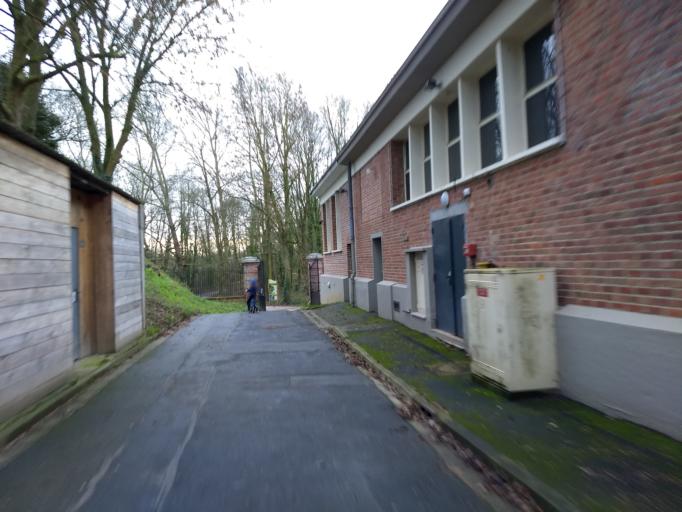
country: FR
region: Nord-Pas-de-Calais
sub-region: Departement du Pas-de-Calais
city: Achicourt
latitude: 50.2833
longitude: 2.7626
